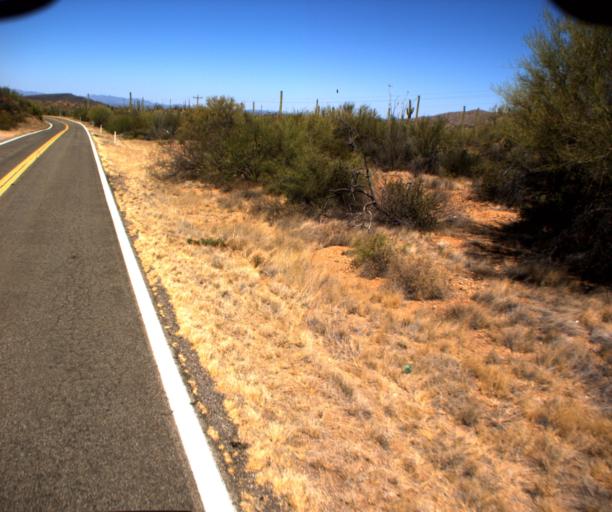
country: US
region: Arizona
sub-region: Pima County
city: Sells
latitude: 32.1752
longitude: -112.1972
